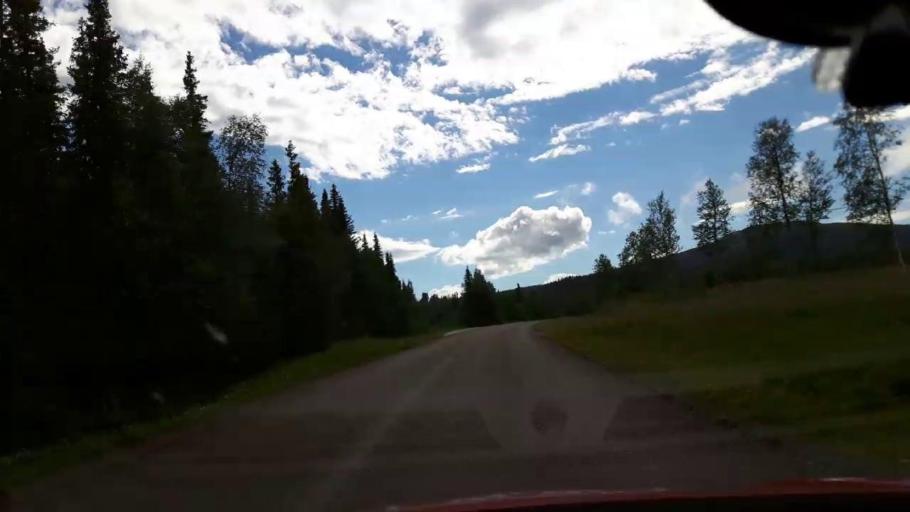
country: SE
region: Jaemtland
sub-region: Are Kommun
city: Are
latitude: 63.3069
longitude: 13.2261
